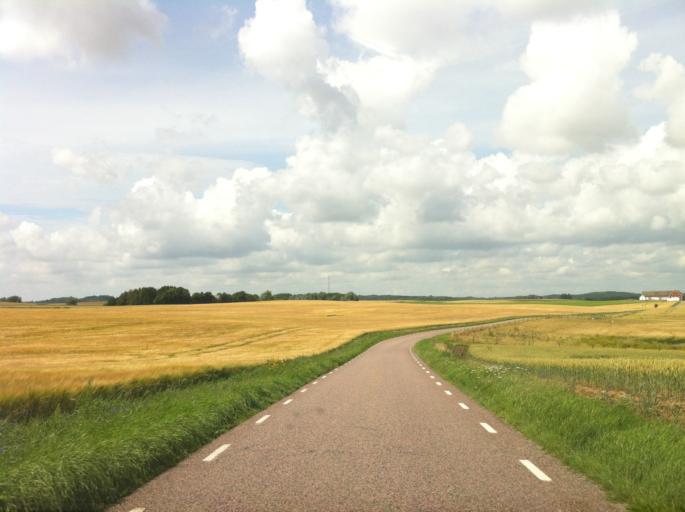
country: SE
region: Skane
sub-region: Skurups Kommun
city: Skurup
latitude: 55.4241
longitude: 13.4485
